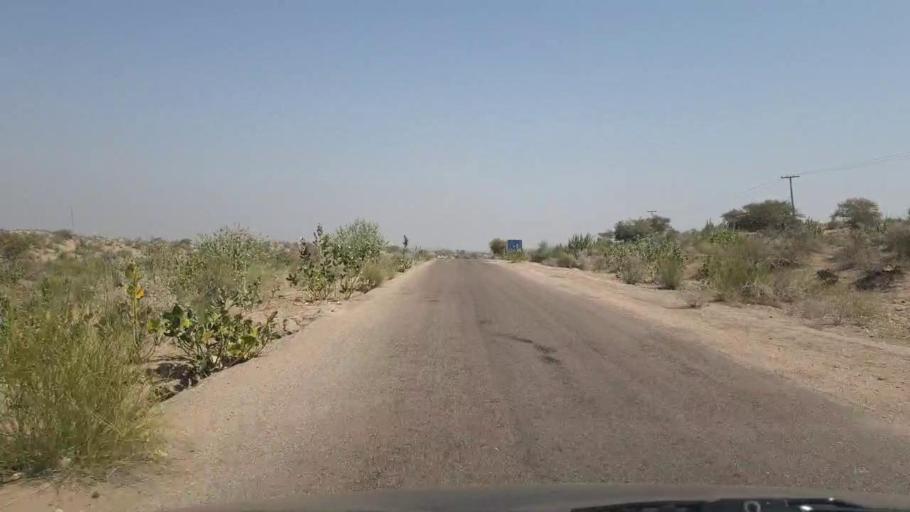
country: PK
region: Sindh
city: Chor
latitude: 25.6373
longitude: 70.0795
